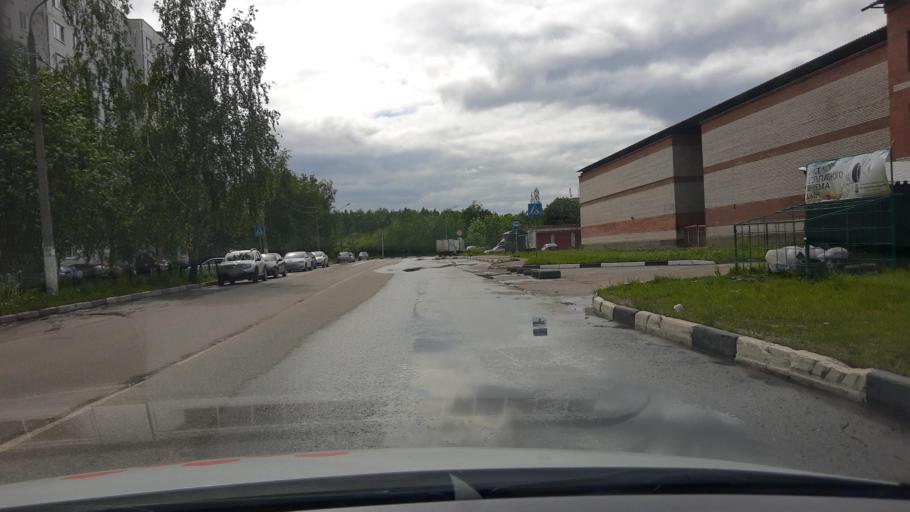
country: RU
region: Moskovskaya
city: Elektrostal'
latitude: 55.7743
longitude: 38.4228
